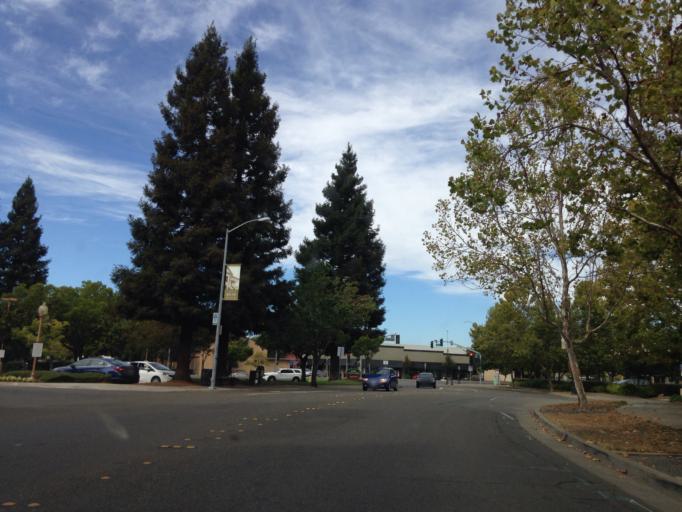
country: US
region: California
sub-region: Sonoma County
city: Santa Rosa
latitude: 38.4355
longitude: -122.7201
